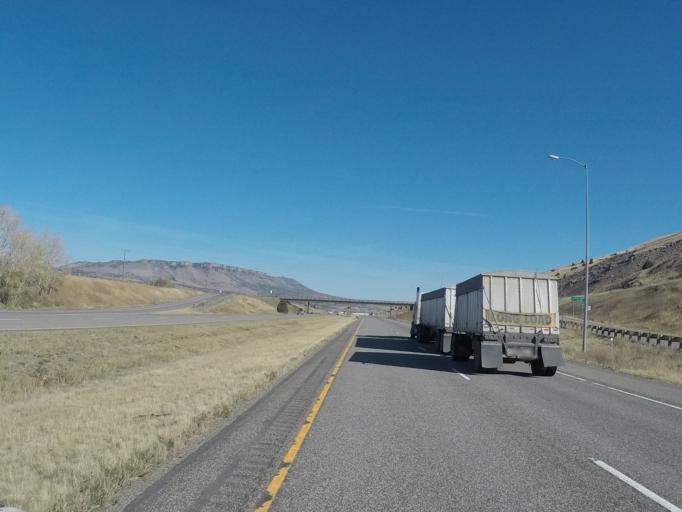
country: US
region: Montana
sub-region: Park County
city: Livingston
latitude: 45.7054
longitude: -110.4582
